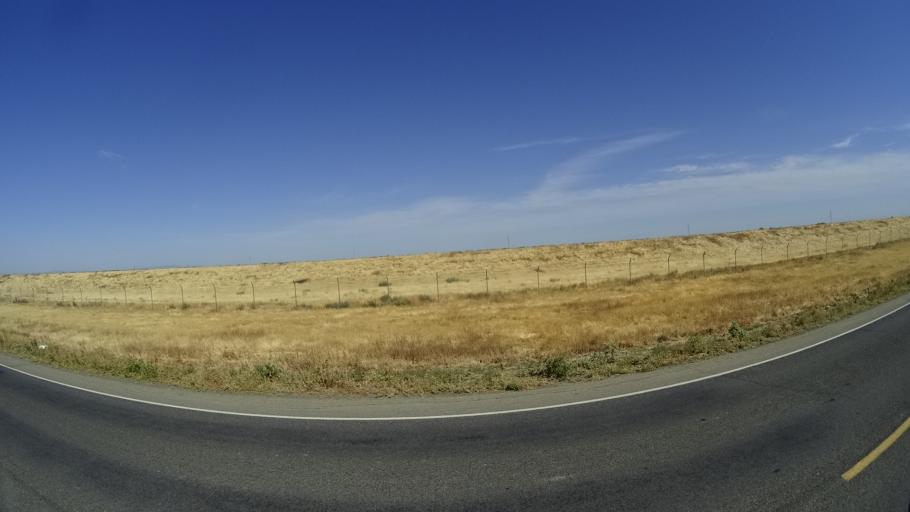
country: US
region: California
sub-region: Kings County
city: Lemoore Station
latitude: 36.2390
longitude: -119.8819
